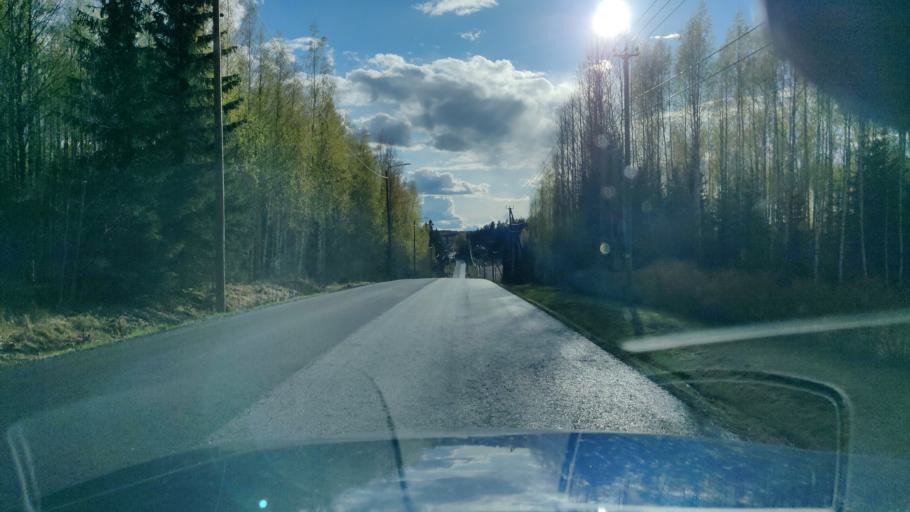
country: FI
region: Uusimaa
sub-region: Helsinki
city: Nurmijaervi
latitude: 60.3591
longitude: 24.7147
